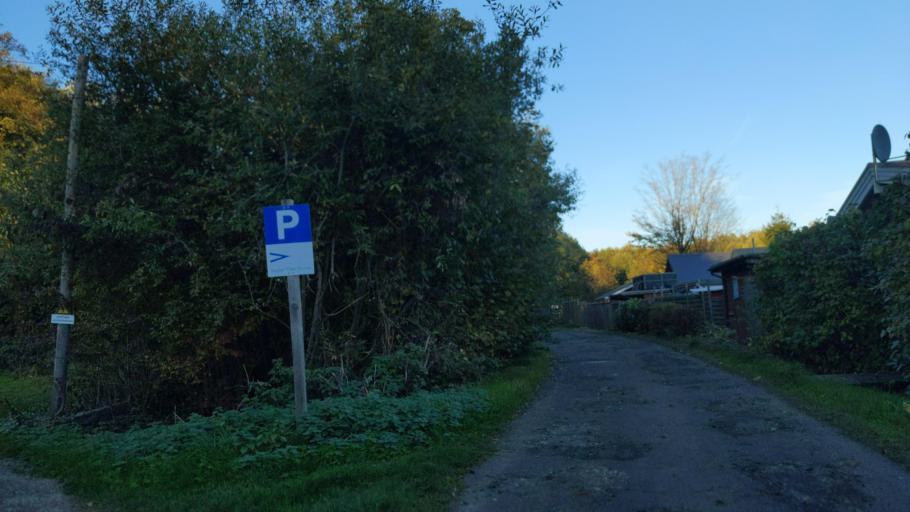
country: DE
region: Schleswig-Holstein
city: Gross Gronau
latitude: 53.7797
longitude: 10.7562
